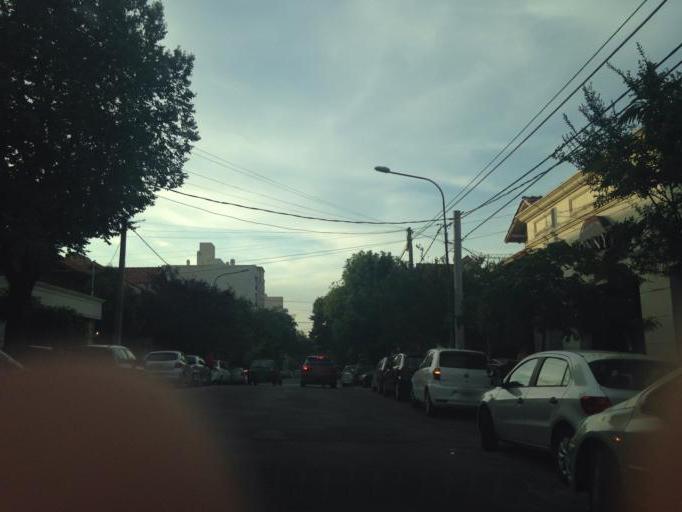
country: AR
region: Buenos Aires
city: Mar del Plata
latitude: -38.0186
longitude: -57.5445
